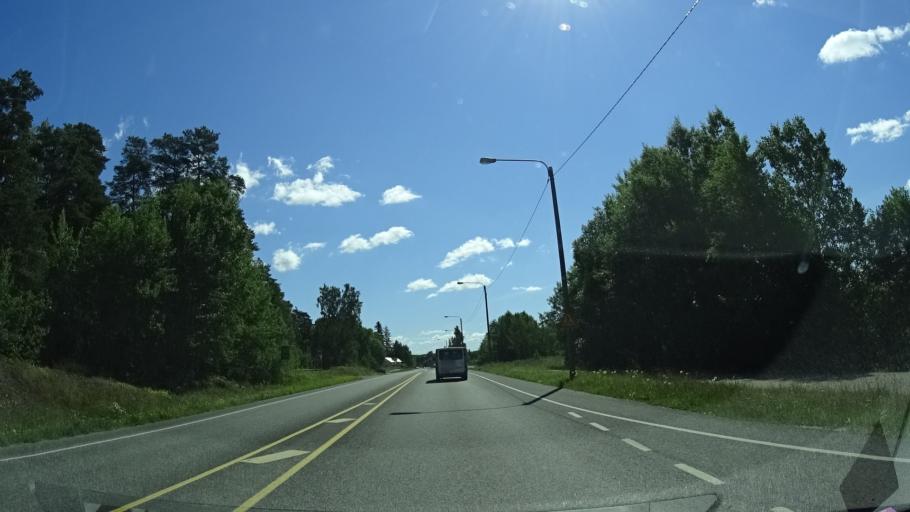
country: FI
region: Varsinais-Suomi
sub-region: Turku
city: Raisio
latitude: 60.5057
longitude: 22.1378
